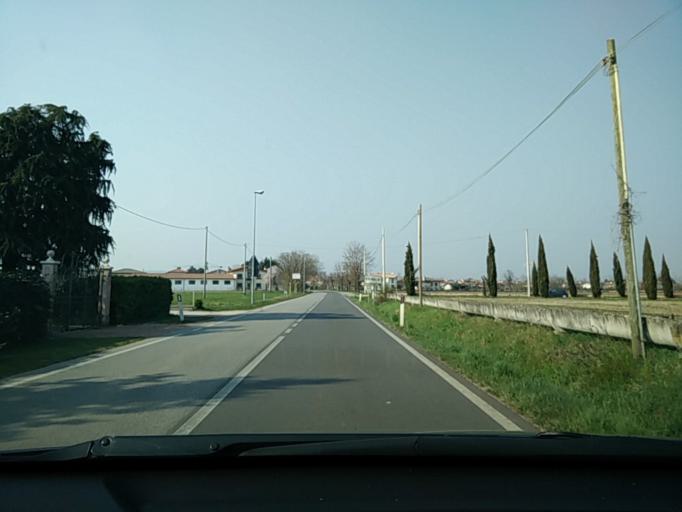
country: IT
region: Veneto
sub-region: Provincia di Treviso
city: Camalo
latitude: 45.7441
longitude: 12.1753
